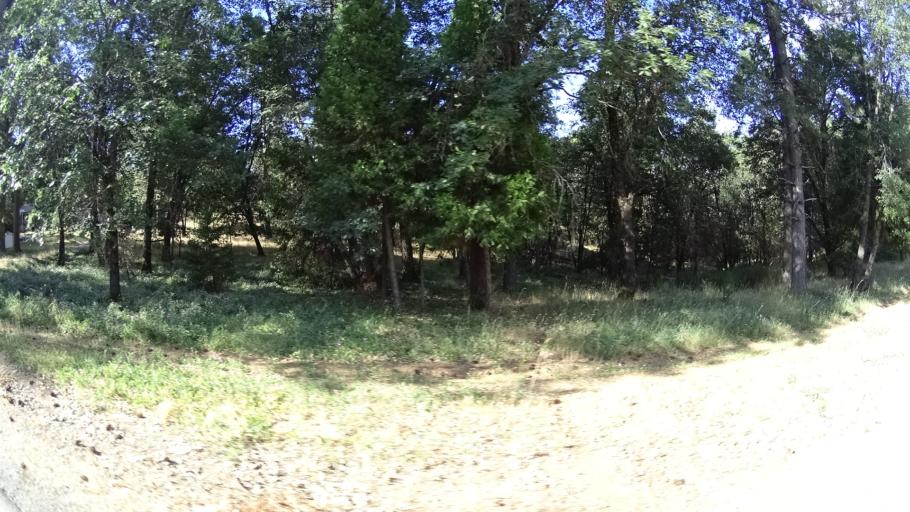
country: US
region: California
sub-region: Amador County
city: Pioneer
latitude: 38.3787
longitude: -120.5138
